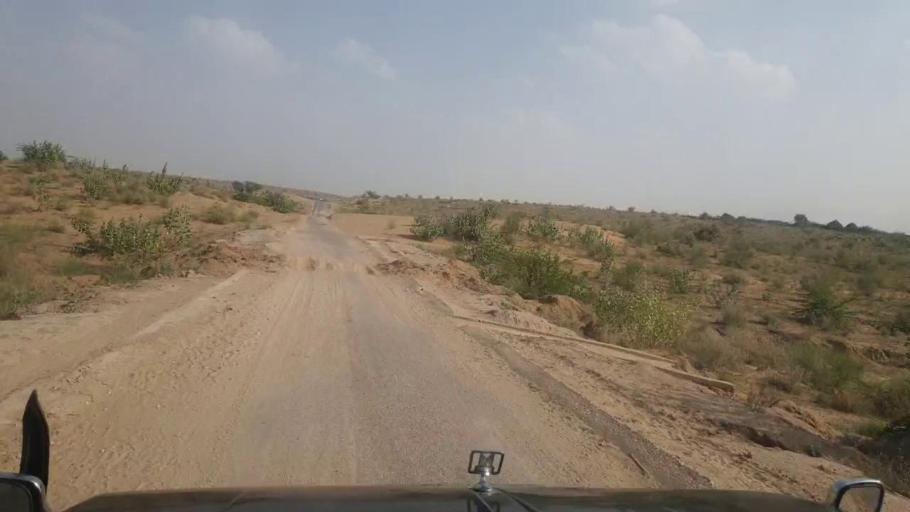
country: PK
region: Sindh
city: Islamkot
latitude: 25.1396
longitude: 70.3178
